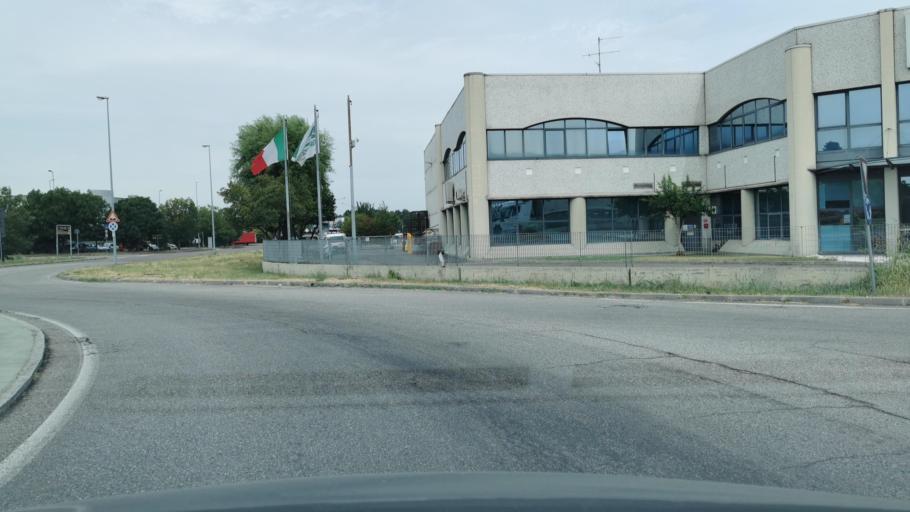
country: IT
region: Emilia-Romagna
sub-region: Provincia di Modena
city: Campogalliano
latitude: 44.6841
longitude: 10.8580
